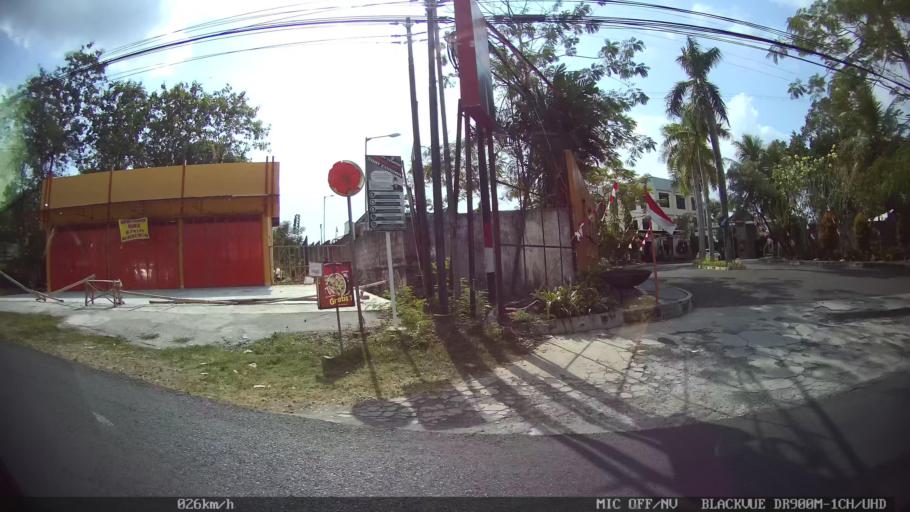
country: ID
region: Daerah Istimewa Yogyakarta
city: Kasihan
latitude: -7.8320
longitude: 110.3143
